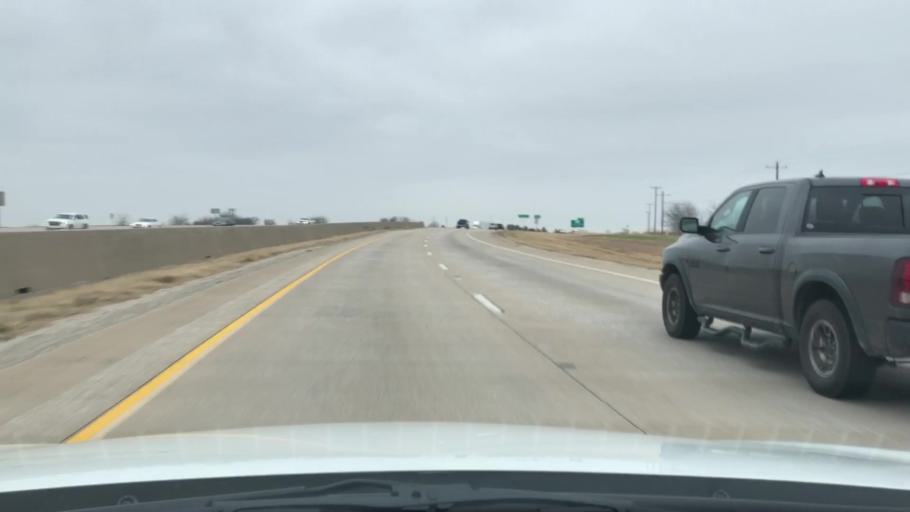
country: US
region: Texas
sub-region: Denton County
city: Sanger
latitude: 33.4233
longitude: -97.1755
